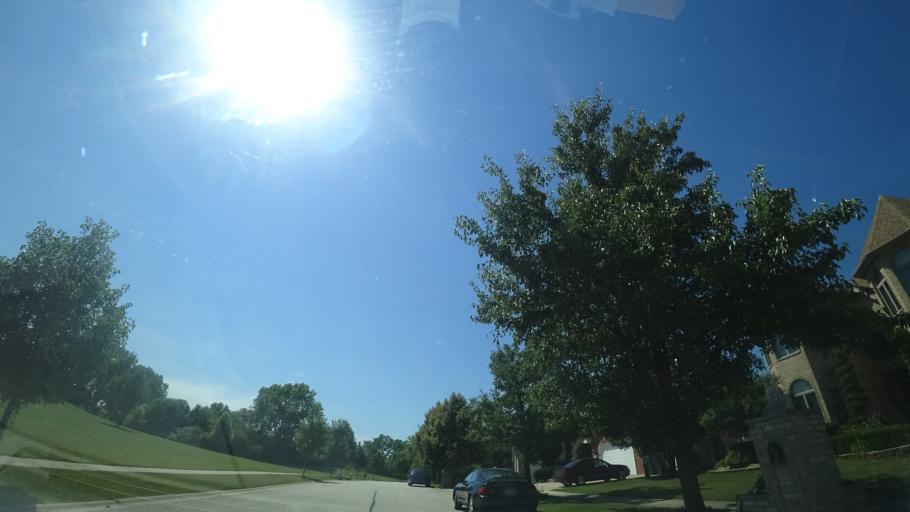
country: US
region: Illinois
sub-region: Will County
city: Mokena
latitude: 41.5609
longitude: -87.8954
